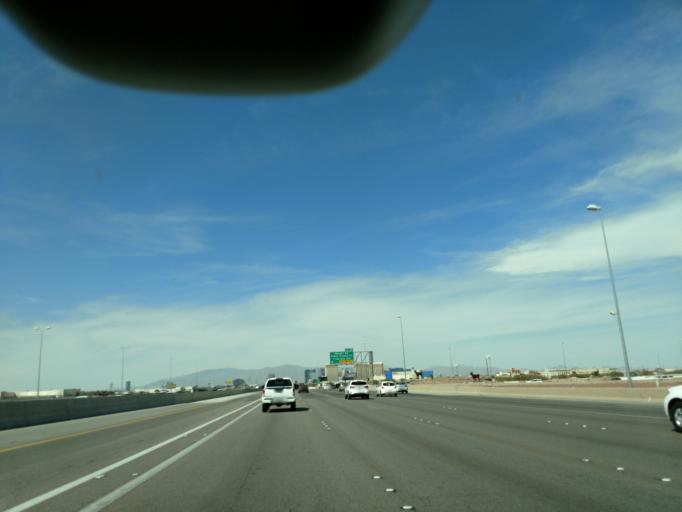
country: US
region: Nevada
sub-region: Clark County
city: Paradise
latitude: 36.0603
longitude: -115.1808
